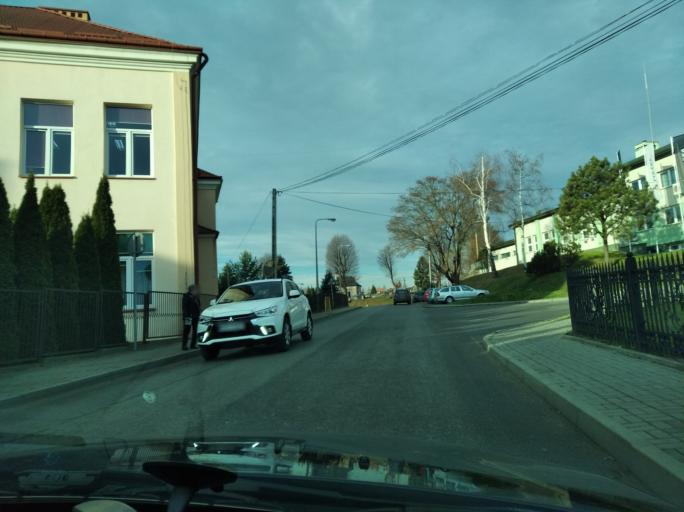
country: PL
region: Subcarpathian Voivodeship
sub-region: Powiat strzyzowski
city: Strzyzow
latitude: 49.8710
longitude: 21.7863
